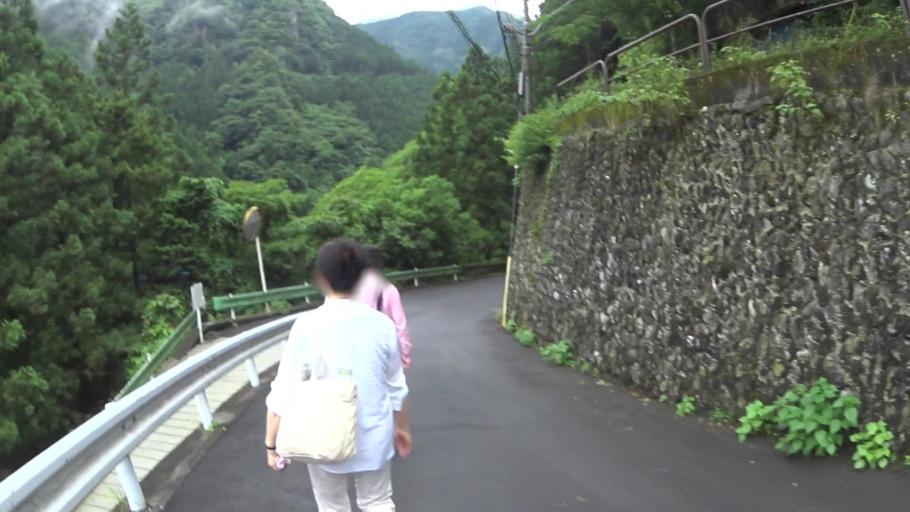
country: JP
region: Tokyo
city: Itsukaichi
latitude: 35.7989
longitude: 139.0781
